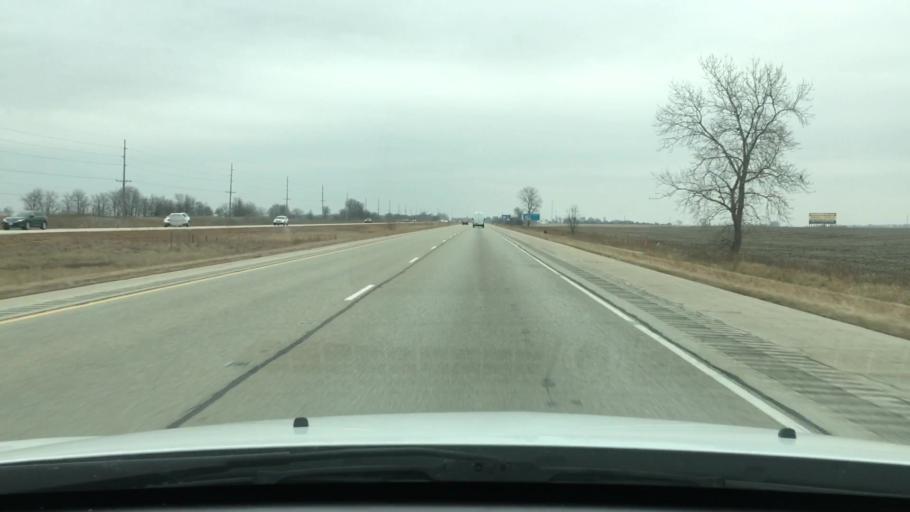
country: US
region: Illinois
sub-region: Logan County
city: Atlanta
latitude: 40.2924
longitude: -89.1942
